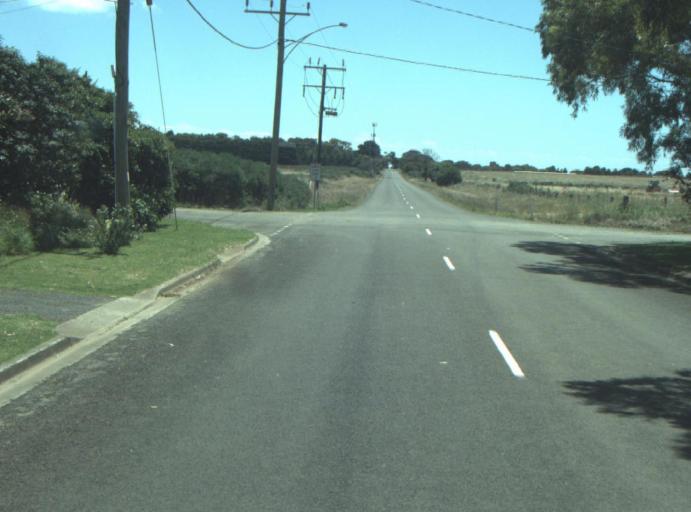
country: AU
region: Victoria
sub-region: Queenscliffe
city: Queenscliff
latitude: -38.1744
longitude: 144.7011
